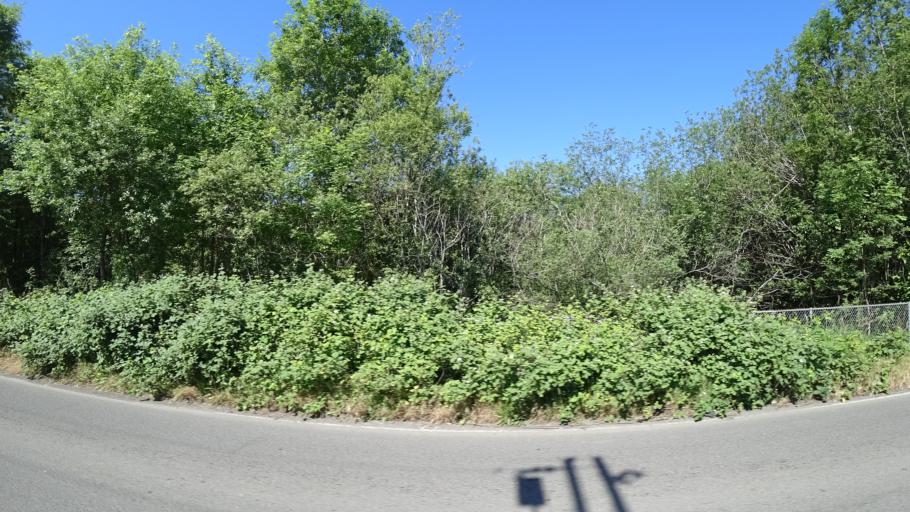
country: US
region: Oregon
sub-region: Multnomah County
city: Lents
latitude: 45.4792
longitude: -122.5490
